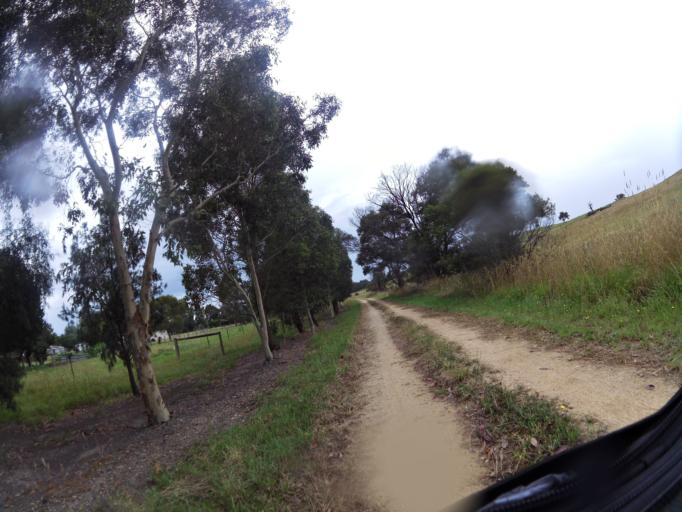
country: AU
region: Victoria
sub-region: East Gippsland
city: Bairnsdale
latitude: -37.7260
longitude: 147.8061
